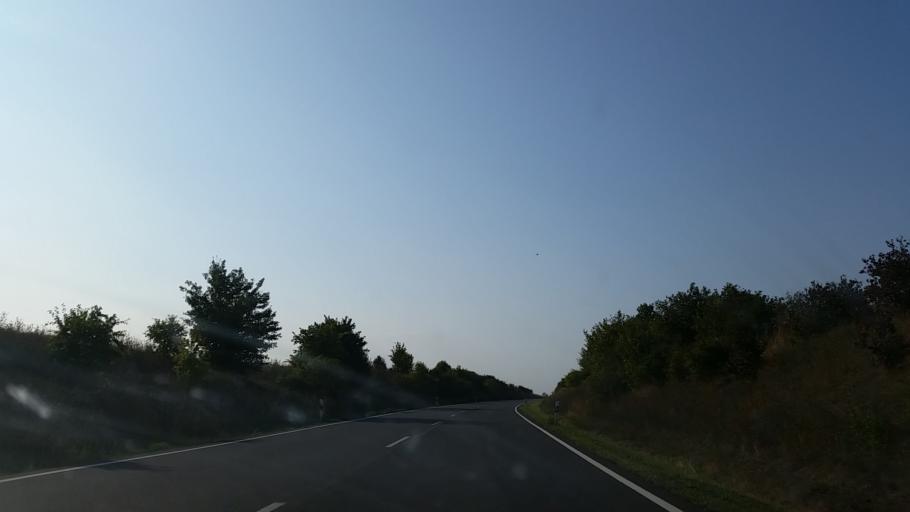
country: DE
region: Brandenburg
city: Zichow
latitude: 53.1988
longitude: 14.0333
